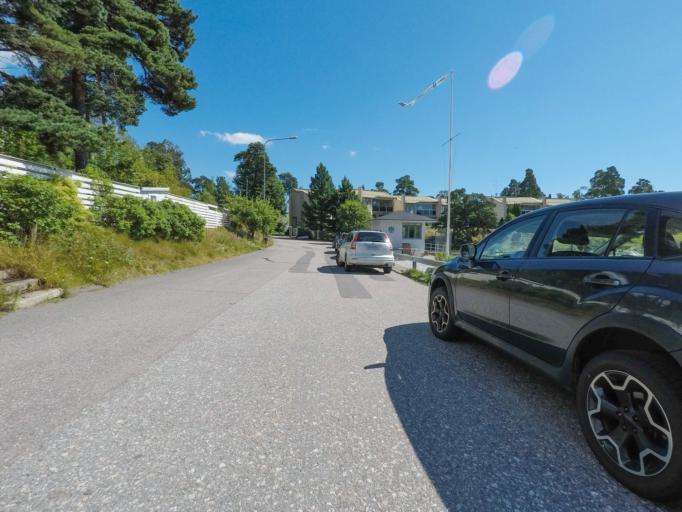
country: FI
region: Uusimaa
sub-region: Helsinki
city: Vantaa
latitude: 60.1881
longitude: 25.0662
